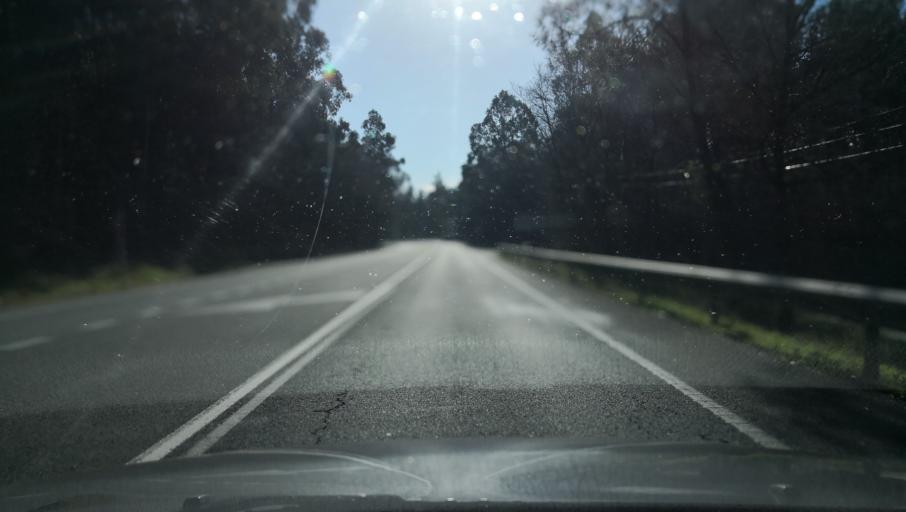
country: ES
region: Galicia
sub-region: Provincia da Coruna
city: Vedra
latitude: 42.7921
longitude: -8.4597
